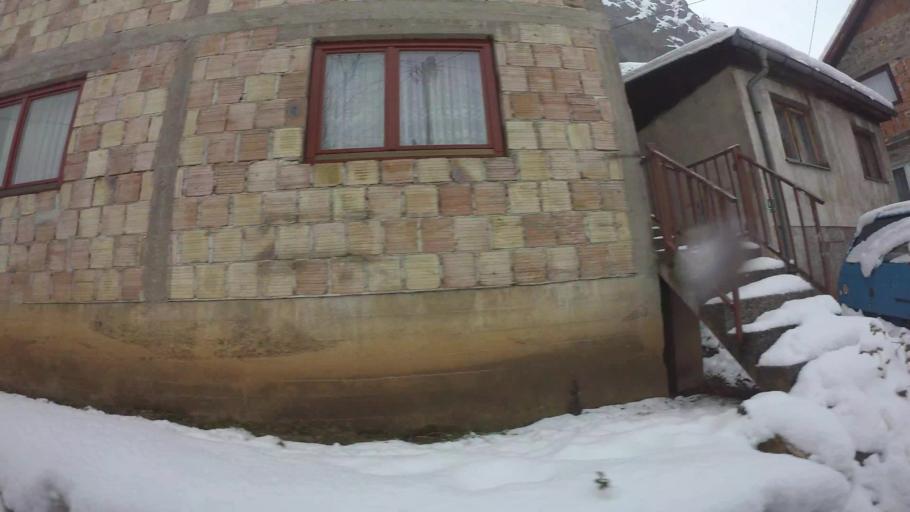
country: BA
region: Federation of Bosnia and Herzegovina
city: Kobilja Glava
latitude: 43.8477
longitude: 18.4155
